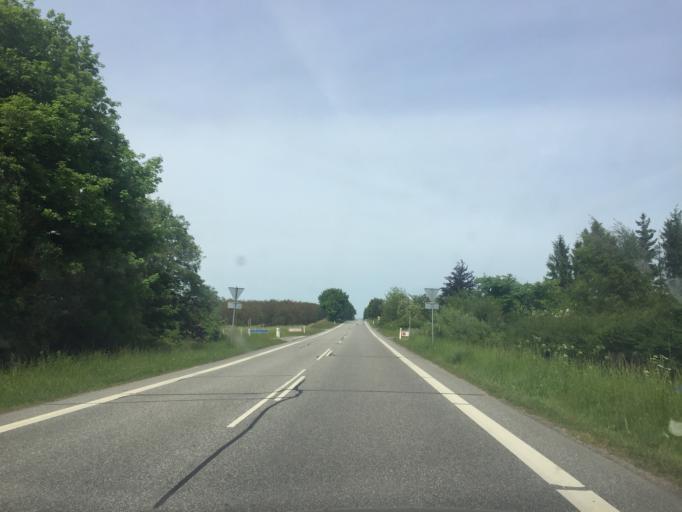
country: DK
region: South Denmark
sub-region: Nyborg Kommune
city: Nyborg
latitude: 55.3075
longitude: 10.7272
